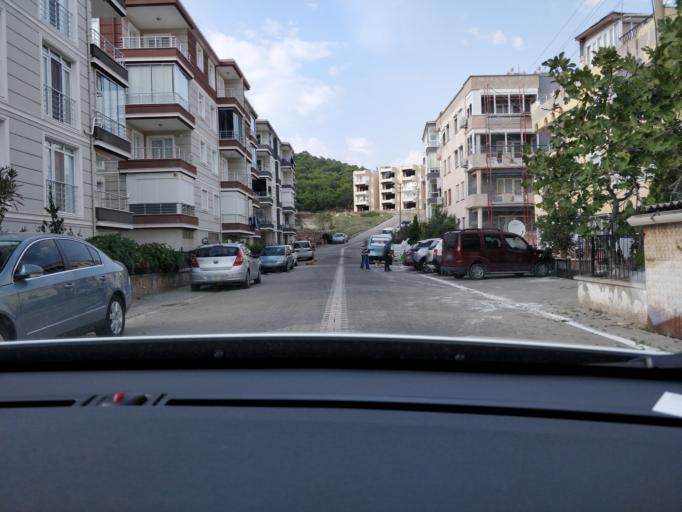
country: TR
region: Balikesir
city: Ayvalik
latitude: 39.2725
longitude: 26.6503
